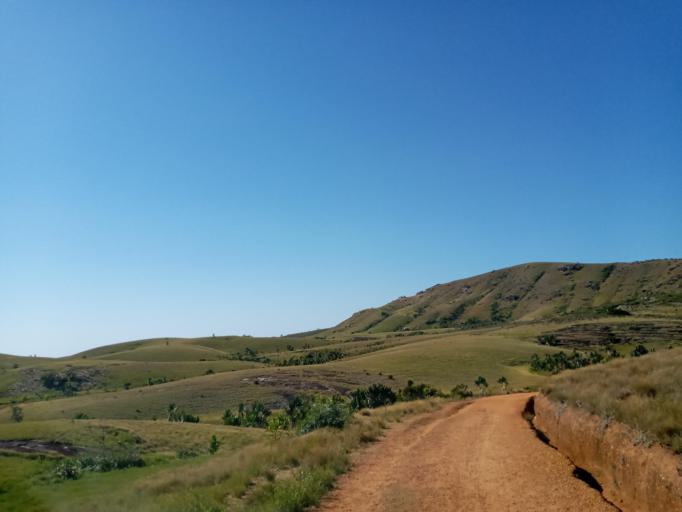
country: MG
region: Anosy
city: Fort Dauphin
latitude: -24.9094
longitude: 47.0755
